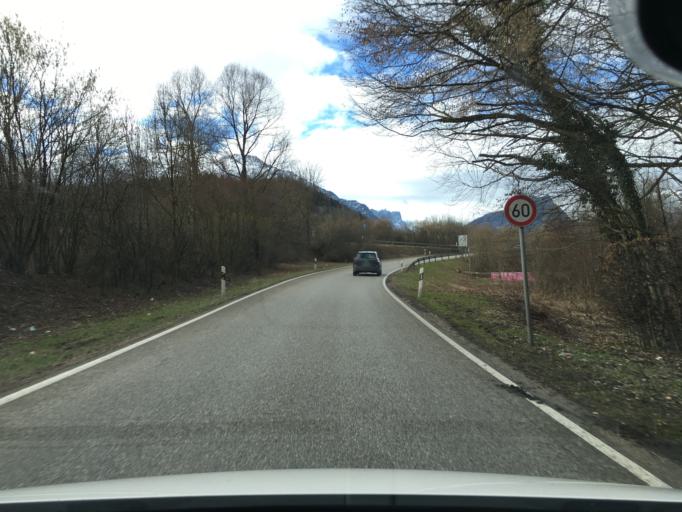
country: DE
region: Bavaria
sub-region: Upper Bavaria
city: Piding
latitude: 47.7448
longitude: 12.9059
